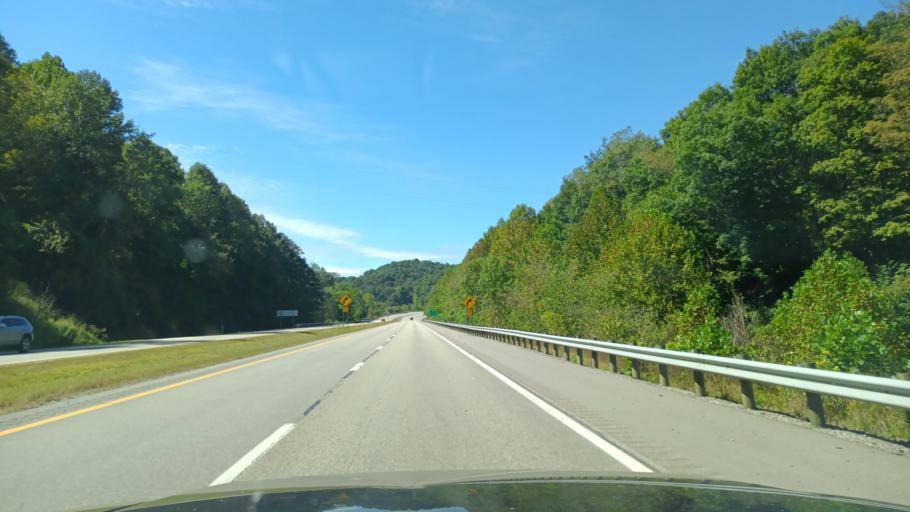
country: US
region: West Virginia
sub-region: Harrison County
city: Salem
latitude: 39.2894
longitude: -80.4911
